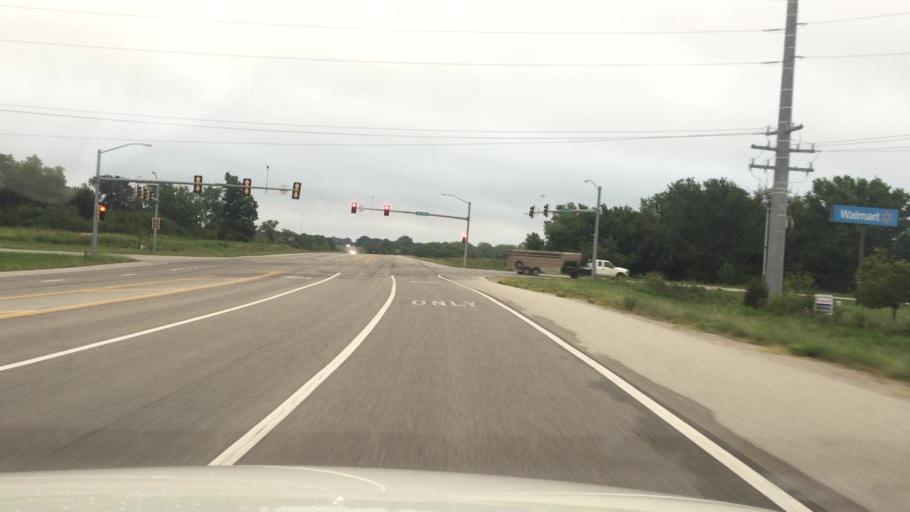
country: US
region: Kansas
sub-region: Montgomery County
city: Coffeyville
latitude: 37.0448
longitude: -95.5786
